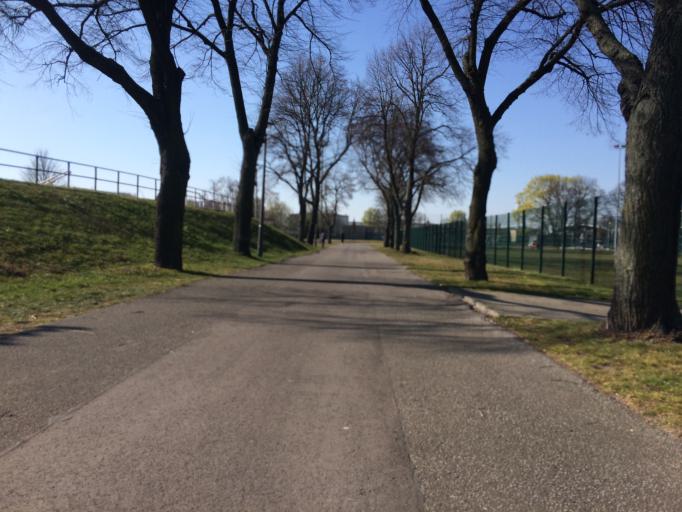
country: DE
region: Berlin
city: Fennpfuhl
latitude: 52.5410
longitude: 13.4779
